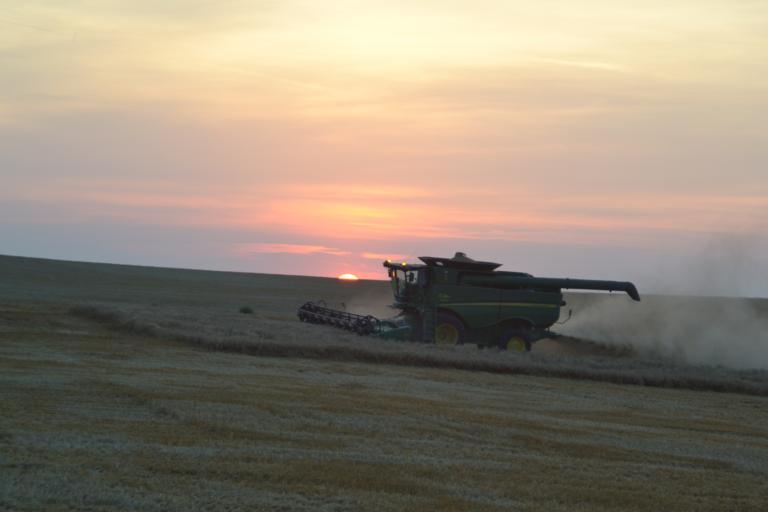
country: US
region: North Dakota
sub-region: Hettinger County
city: Mott
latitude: 46.4446
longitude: -102.5507
